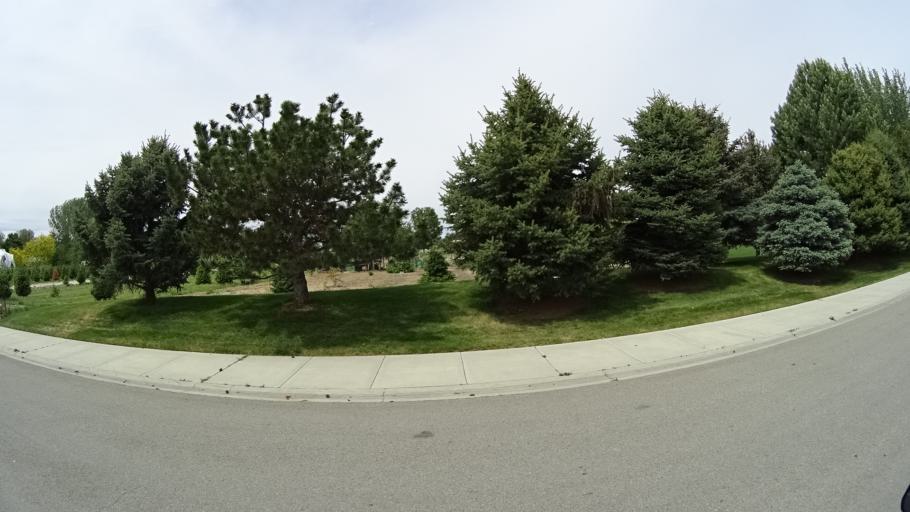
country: US
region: Idaho
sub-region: Ada County
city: Meridian
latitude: 43.5454
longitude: -116.3244
